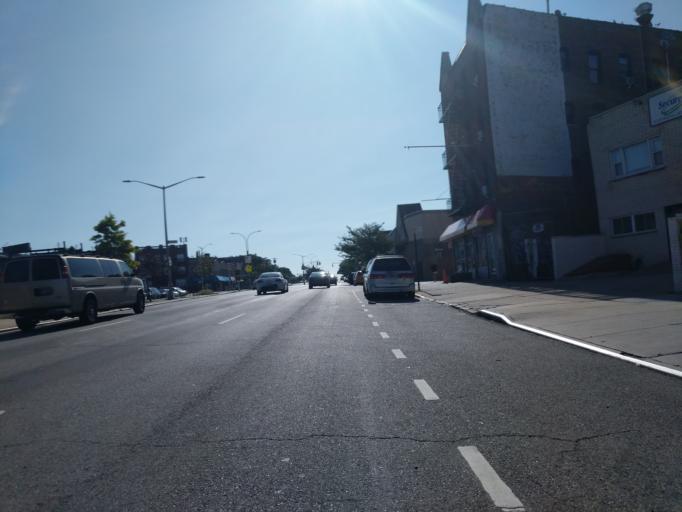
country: US
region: New York
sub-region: Queens County
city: Long Island City
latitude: 40.7632
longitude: -73.8768
